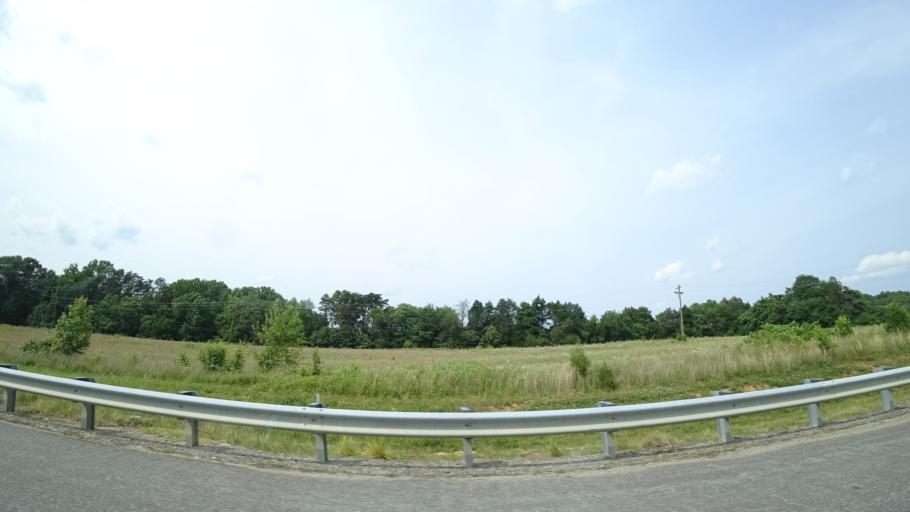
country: US
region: Virginia
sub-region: Spotsylvania County
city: Spotsylvania Courthouse
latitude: 38.1621
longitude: -77.6518
